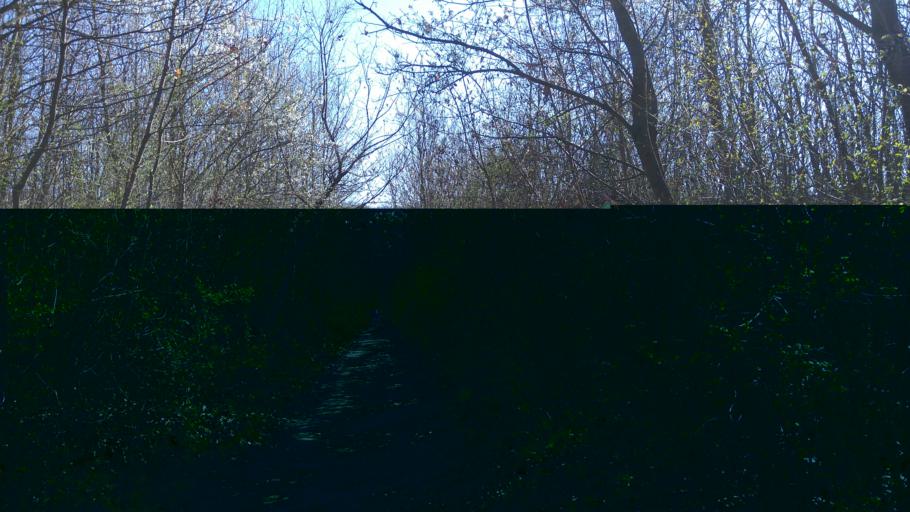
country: HU
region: Pest
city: Budakeszi
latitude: 47.4935
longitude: 18.9405
